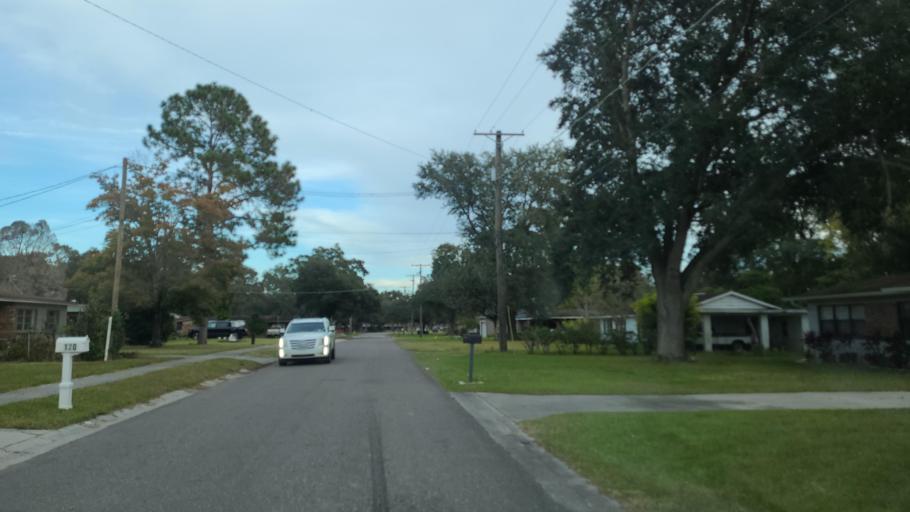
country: US
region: Florida
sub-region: Hillsborough County
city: Brandon
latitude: 27.9419
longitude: -82.2834
